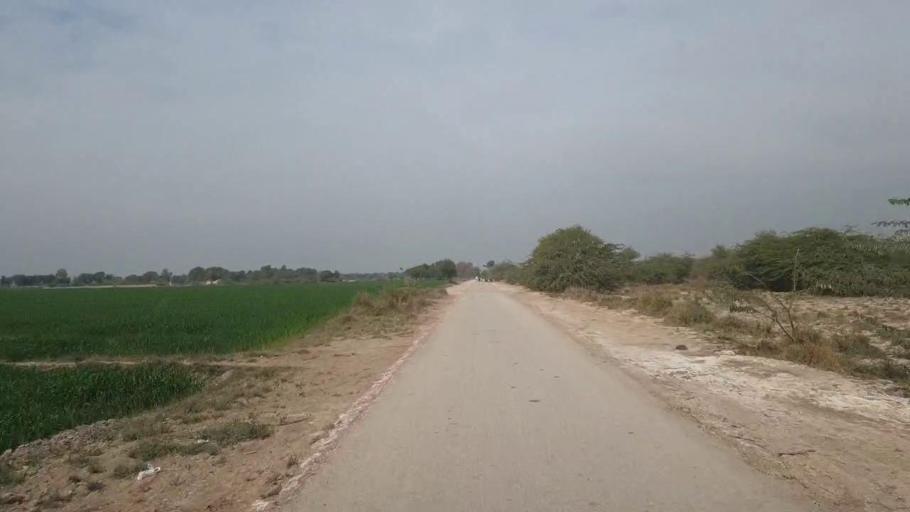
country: PK
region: Sindh
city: Nawabshah
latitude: 26.1104
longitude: 68.4811
